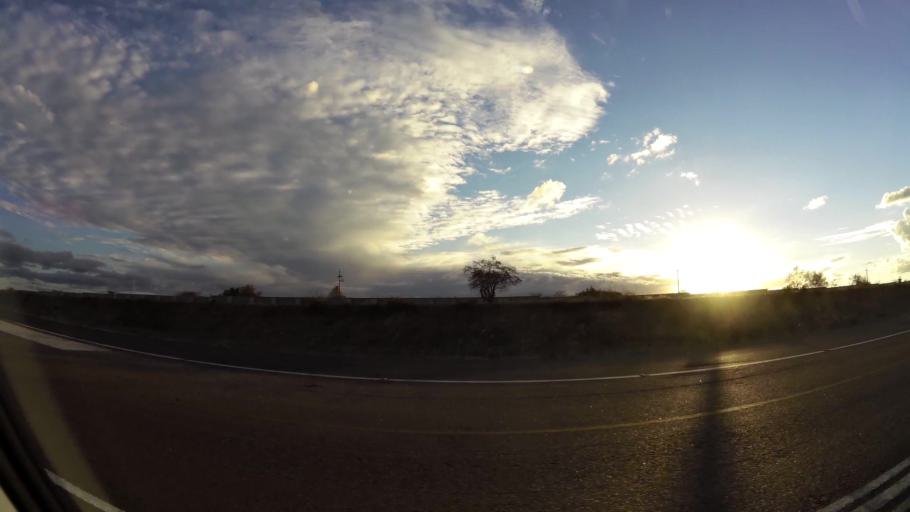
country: ZA
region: Limpopo
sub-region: Capricorn District Municipality
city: Polokwane
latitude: -23.8727
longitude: 29.5072
